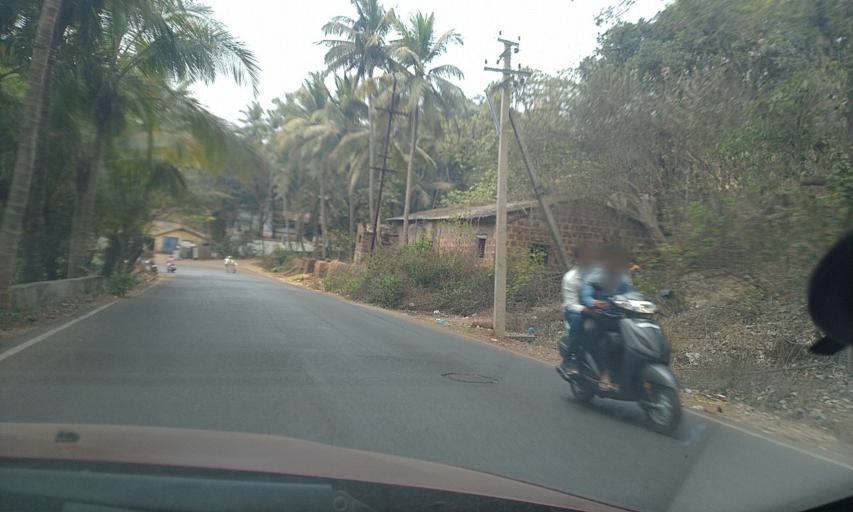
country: IN
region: Goa
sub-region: North Goa
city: Mapuca
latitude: 15.5952
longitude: 73.7994
